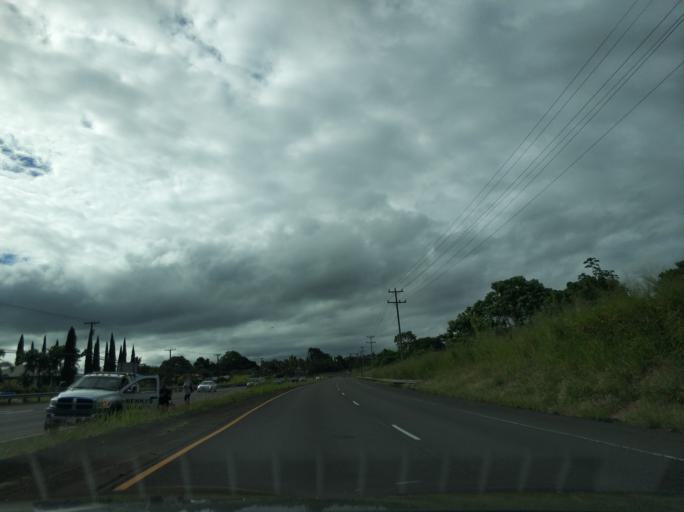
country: US
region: Hawaii
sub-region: Hawaii County
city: Kea'au
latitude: 19.6312
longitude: -155.0399
